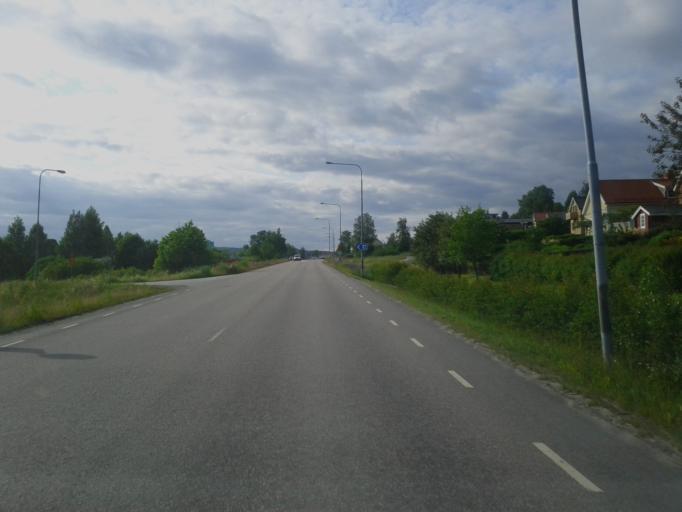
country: SE
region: Vaesternorrland
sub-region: OErnskoeldsviks Kommun
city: Ornskoldsvik
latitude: 63.2793
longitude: 18.7469
